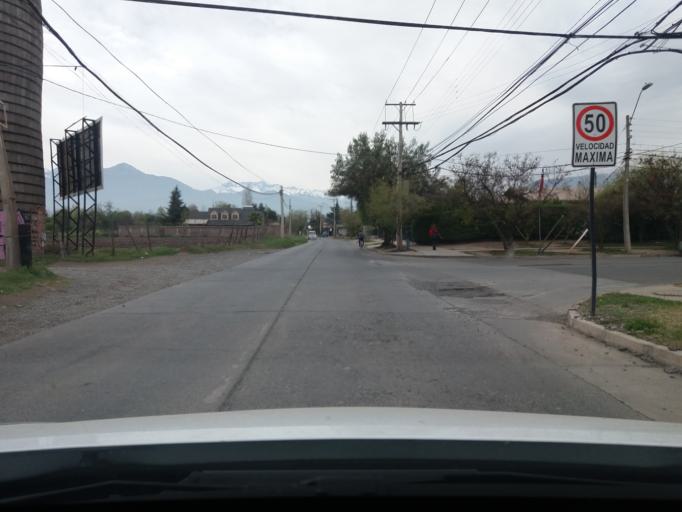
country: CL
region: Valparaiso
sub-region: Provincia de Los Andes
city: Los Andes
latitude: -32.8313
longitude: -70.6156
